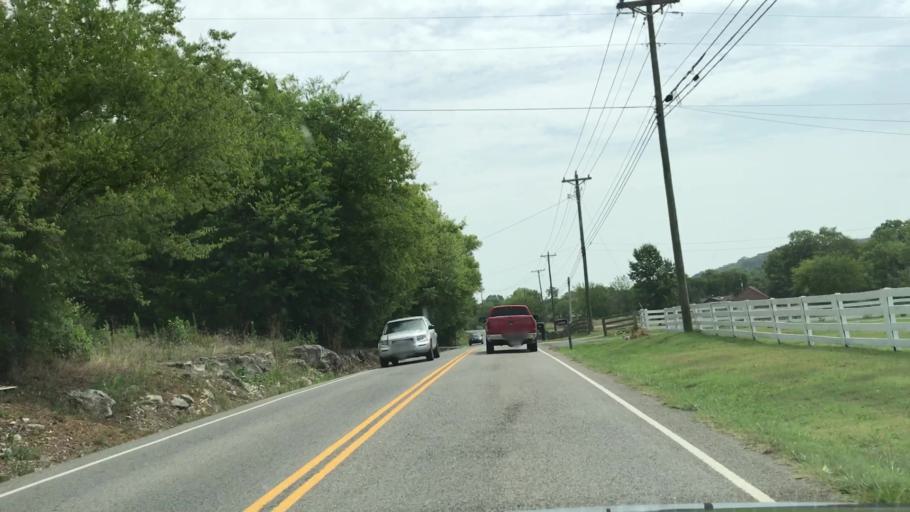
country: US
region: Tennessee
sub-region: Williamson County
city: Nolensville
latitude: 35.9378
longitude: -86.6889
